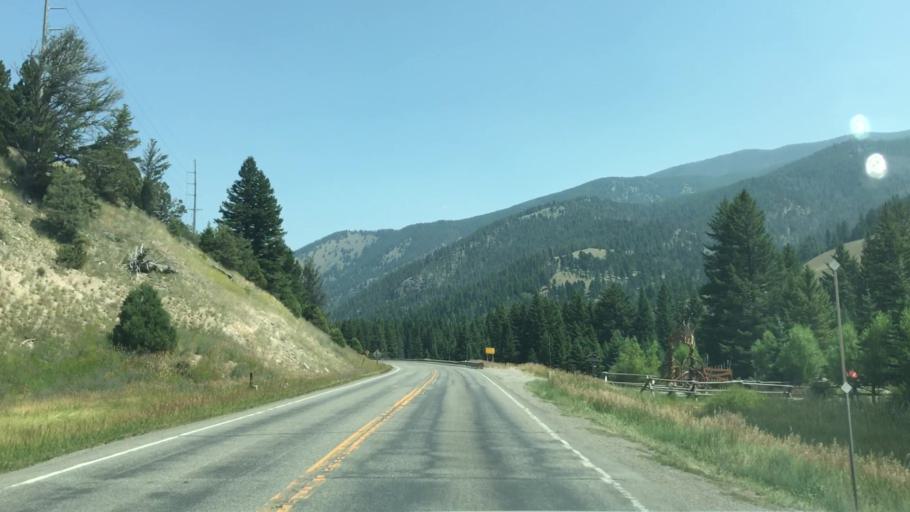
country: US
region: Montana
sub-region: Gallatin County
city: Big Sky
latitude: 45.2700
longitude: -111.2468
